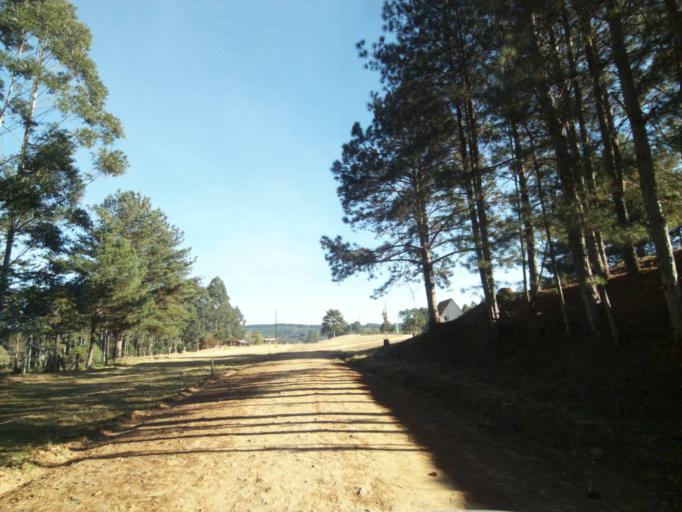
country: BR
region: Parana
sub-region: Telemaco Borba
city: Telemaco Borba
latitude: -24.5143
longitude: -50.6616
